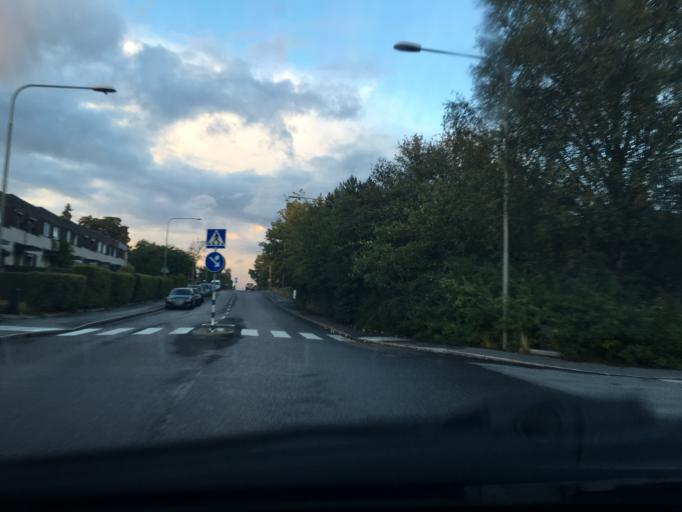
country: SE
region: Stockholm
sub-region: Jarfalla Kommun
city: Jakobsberg
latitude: 59.3746
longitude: 17.8705
